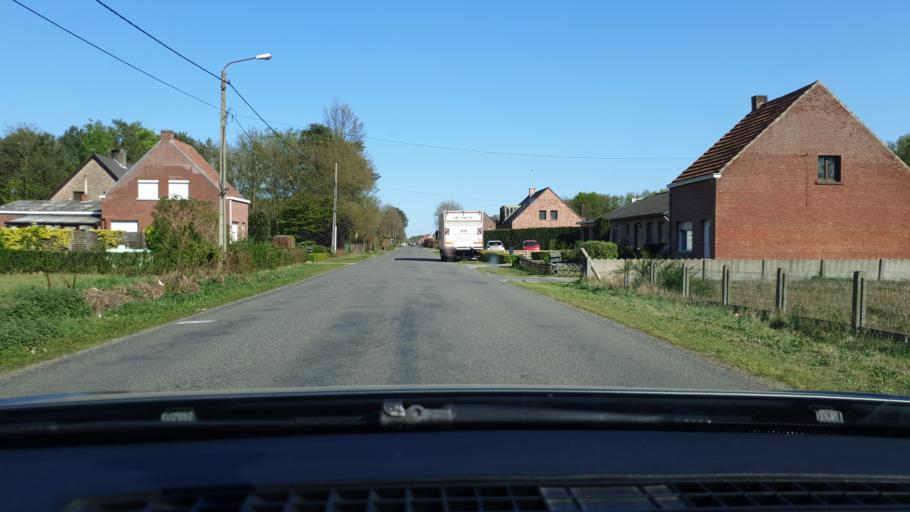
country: BE
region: Flanders
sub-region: Provincie Antwerpen
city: Geel
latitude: 51.1818
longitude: 4.9253
